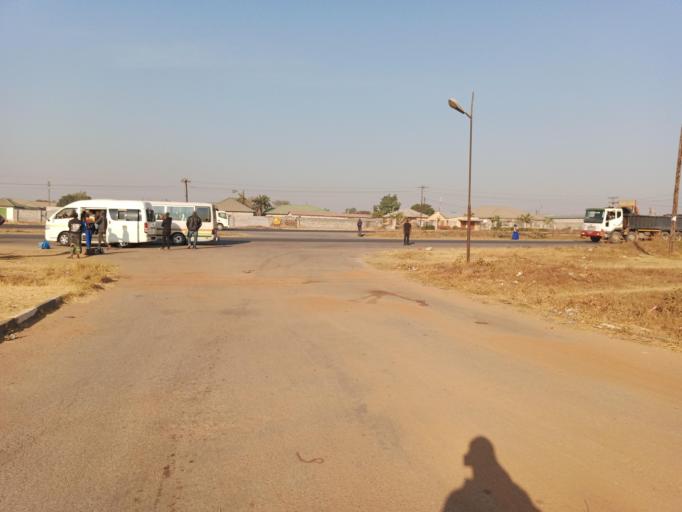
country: ZM
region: Copperbelt
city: Kitwe
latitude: -12.8755
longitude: 28.2526
